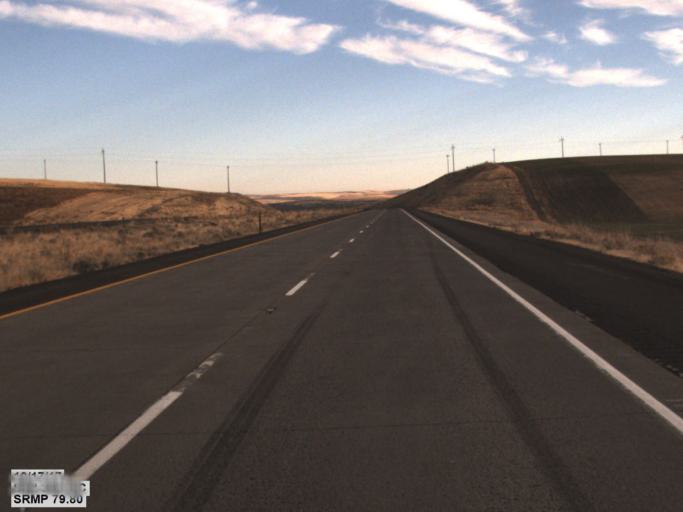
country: US
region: Washington
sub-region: Adams County
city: Ritzville
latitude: 46.9379
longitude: -118.5849
